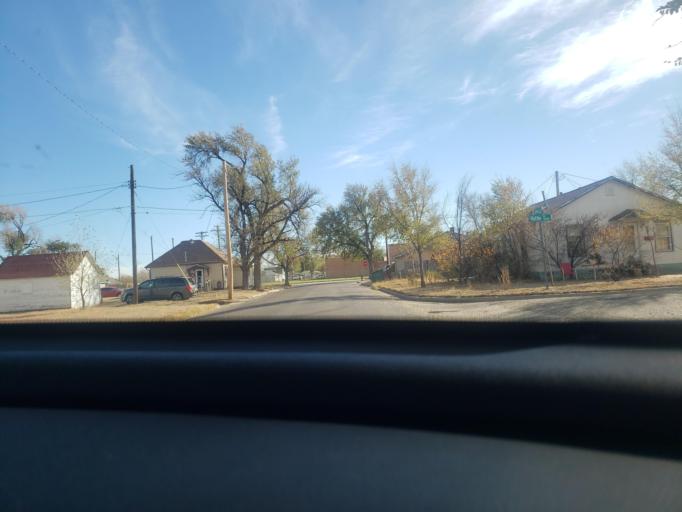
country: US
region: Kansas
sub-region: Finney County
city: Garden City
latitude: 37.9770
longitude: -100.8757
